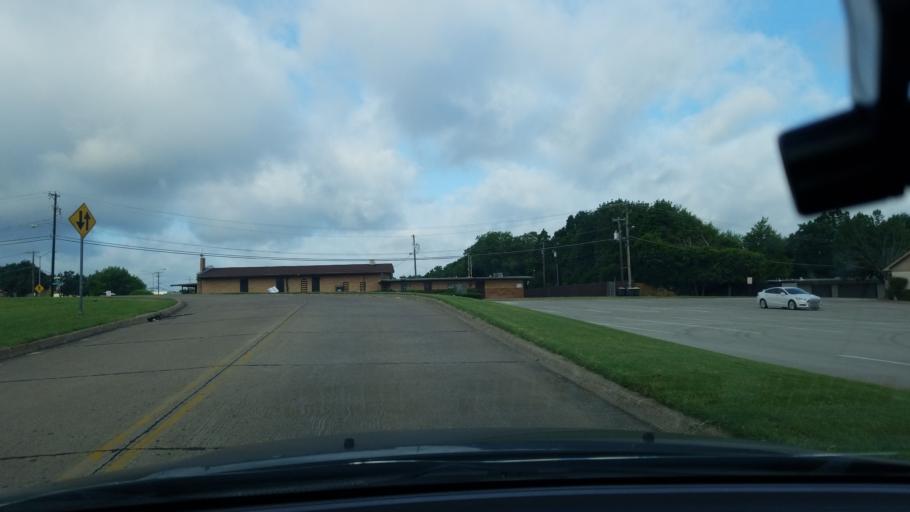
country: US
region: Texas
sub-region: Dallas County
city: Highland Park
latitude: 32.8175
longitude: -96.6905
